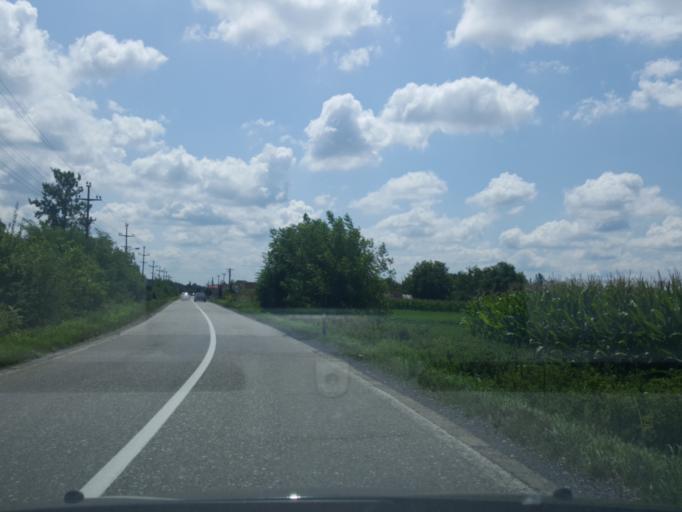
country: RS
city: Metkovic
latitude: 44.8633
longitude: 19.5441
